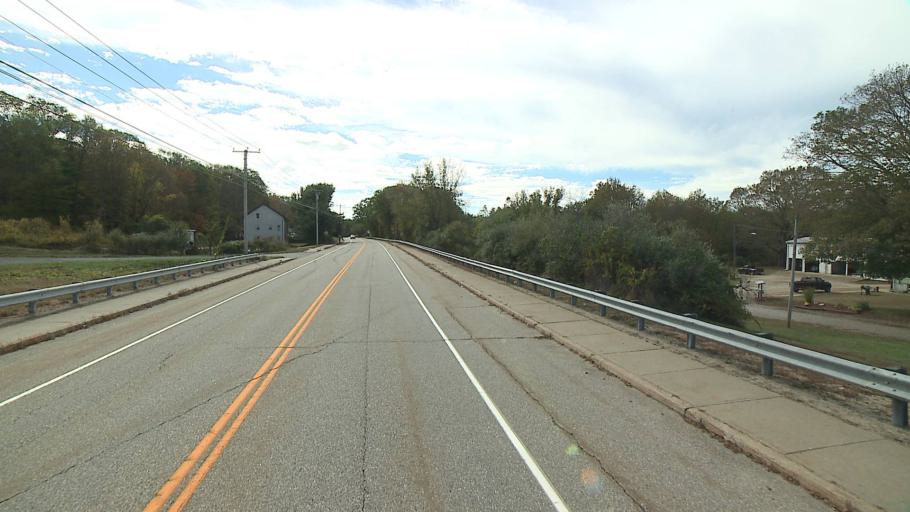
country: US
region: Connecticut
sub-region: Windham County
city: Putnam
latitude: 41.9403
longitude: -71.8941
